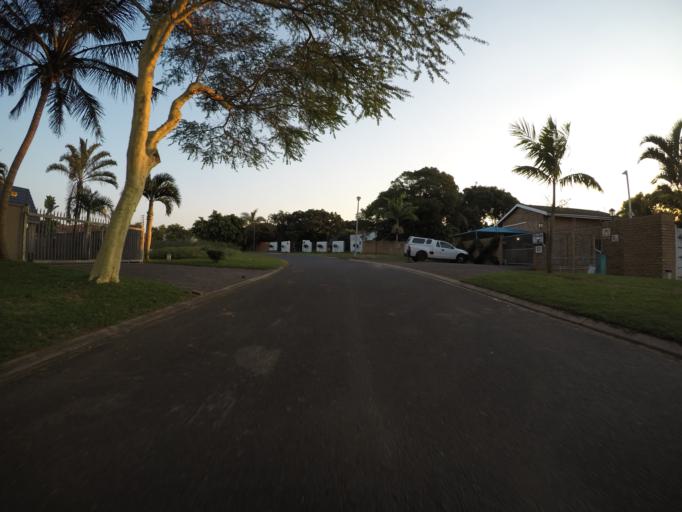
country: ZA
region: KwaZulu-Natal
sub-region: uThungulu District Municipality
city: Richards Bay
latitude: -28.7631
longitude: 32.1201
